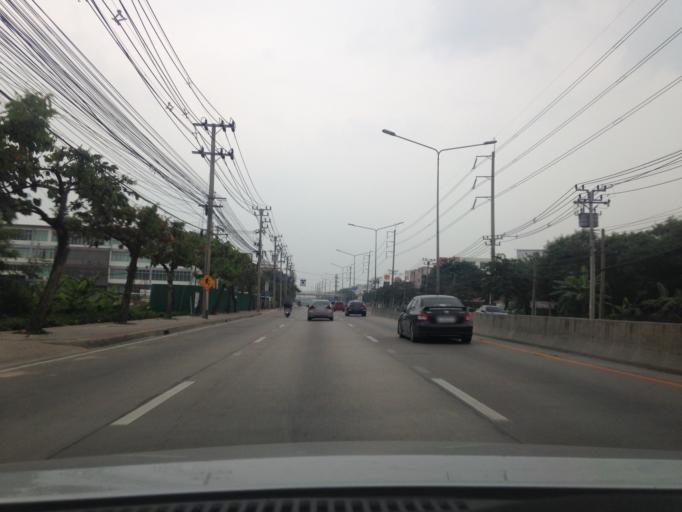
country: TH
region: Bangkok
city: Lat Krabang
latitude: 13.7393
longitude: 100.7465
